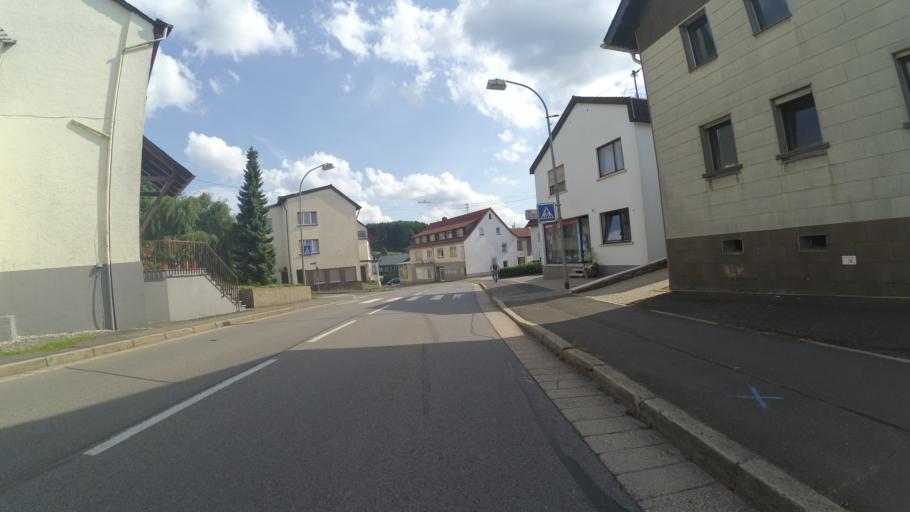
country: DE
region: Rheinland-Pfalz
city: Achtelsbach
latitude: 49.5944
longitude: 7.0649
